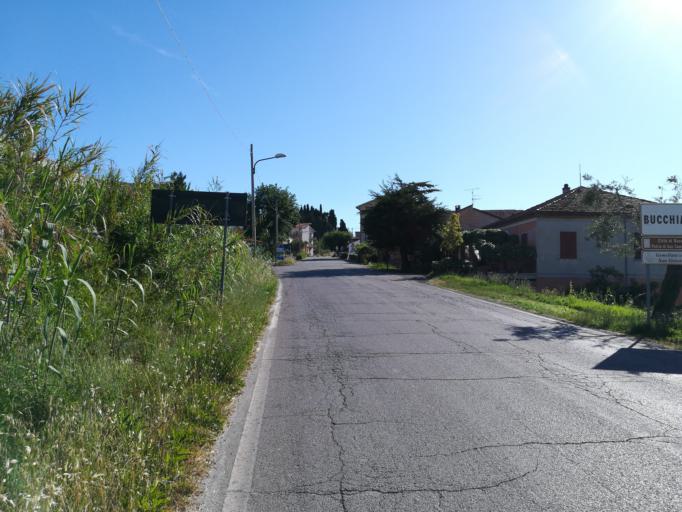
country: IT
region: Abruzzo
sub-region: Provincia di Chieti
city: Bucchianico
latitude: 42.2976
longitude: 14.1735
